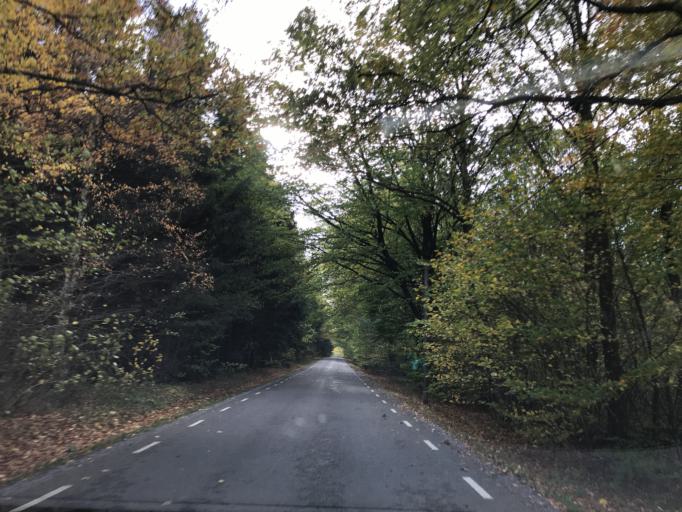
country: SE
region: Skane
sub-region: Bjuvs Kommun
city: Billesholm
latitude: 56.0209
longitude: 13.0020
